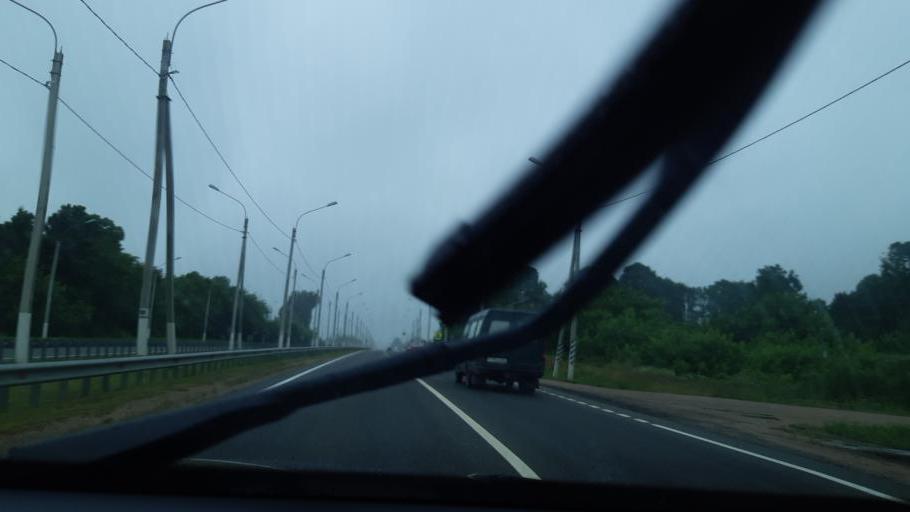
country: RU
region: Smolensk
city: Talashkino
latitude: 54.6402
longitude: 32.1775
